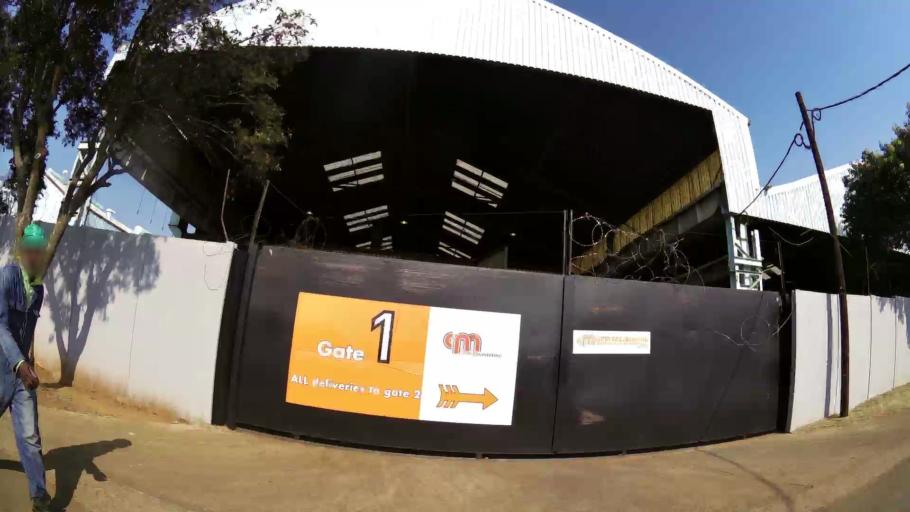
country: ZA
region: Gauteng
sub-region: Ekurhuleni Metropolitan Municipality
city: Germiston
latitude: -26.1632
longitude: 28.1997
